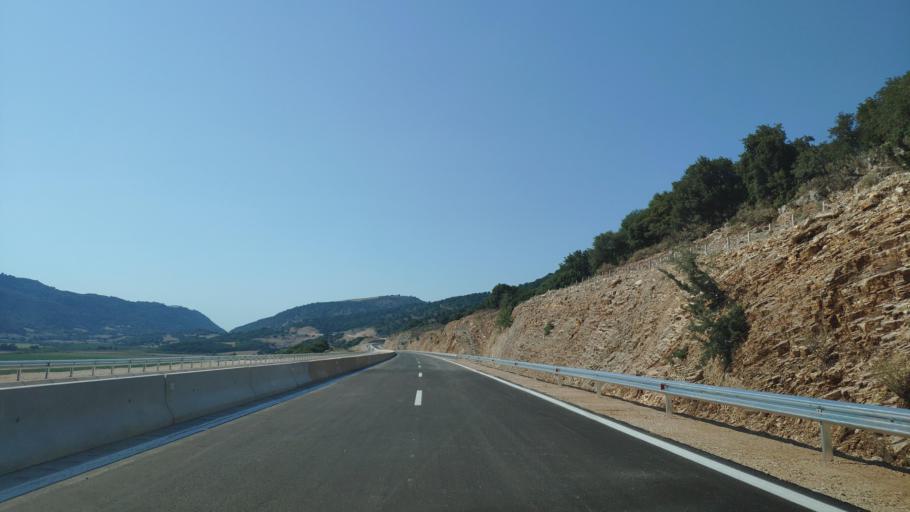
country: GR
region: West Greece
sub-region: Nomos Aitolias kai Akarnanias
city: Katouna
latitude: 38.8256
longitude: 21.1229
